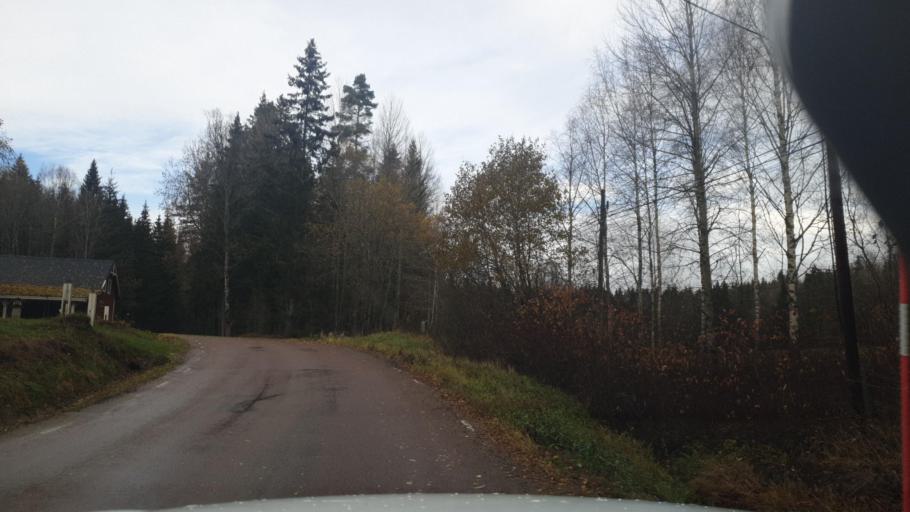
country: NO
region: Hedmark
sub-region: Eidskog
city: Skotterud
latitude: 59.8221
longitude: 12.0033
